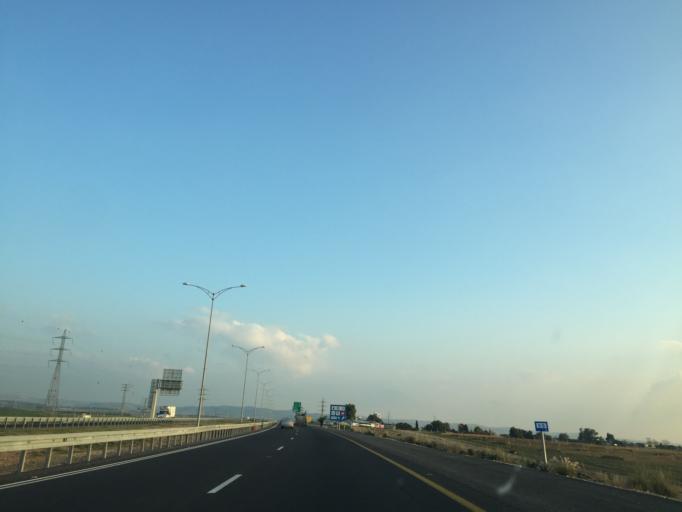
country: IL
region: Southern District
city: Lehavim
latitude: 31.4335
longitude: 34.7752
